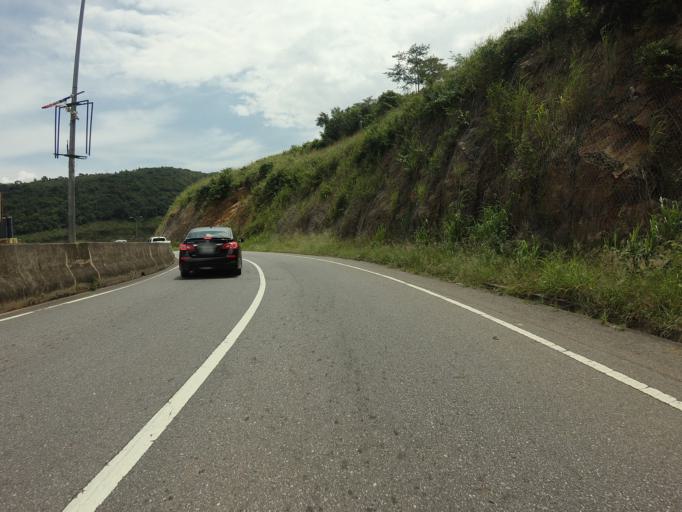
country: GH
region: Eastern
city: Aburi
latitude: 5.7913
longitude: -0.1874
